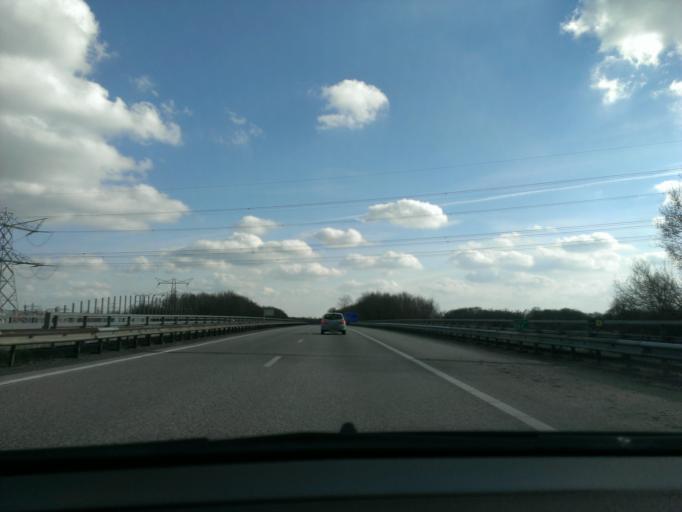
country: NL
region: Overijssel
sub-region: Gemeente Hengelo
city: Hengelo
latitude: 52.2518
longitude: 6.7538
